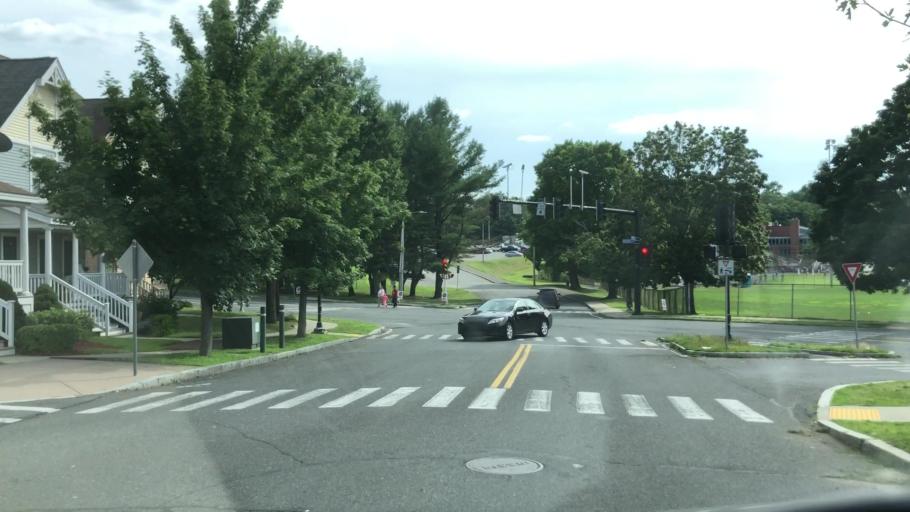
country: US
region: Massachusetts
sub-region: Hampden County
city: Holyoke
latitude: 42.2018
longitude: -72.6196
